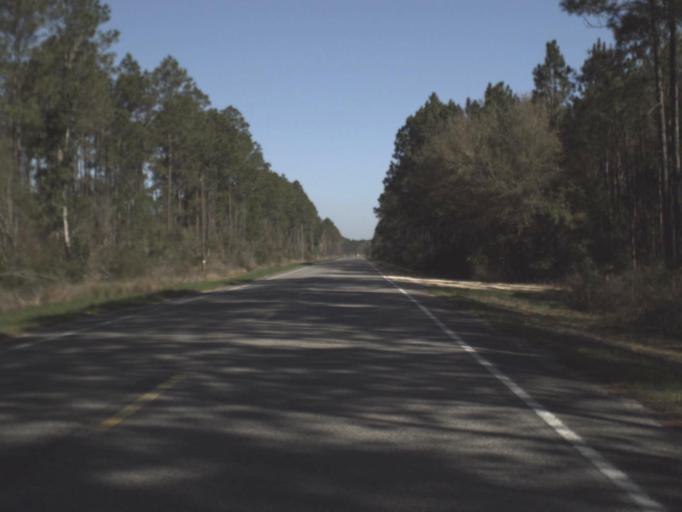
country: US
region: Florida
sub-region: Leon County
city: Woodville
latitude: 30.2967
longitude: -84.0480
